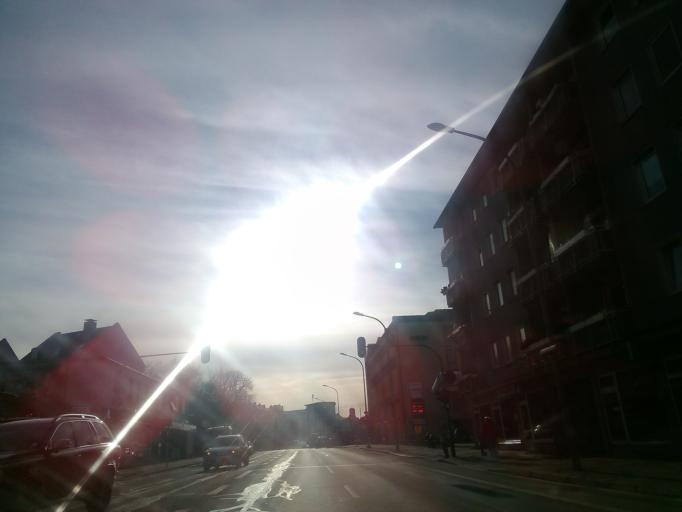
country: DE
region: Bavaria
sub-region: Upper Bavaria
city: Munich
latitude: 48.1147
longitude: 11.5766
